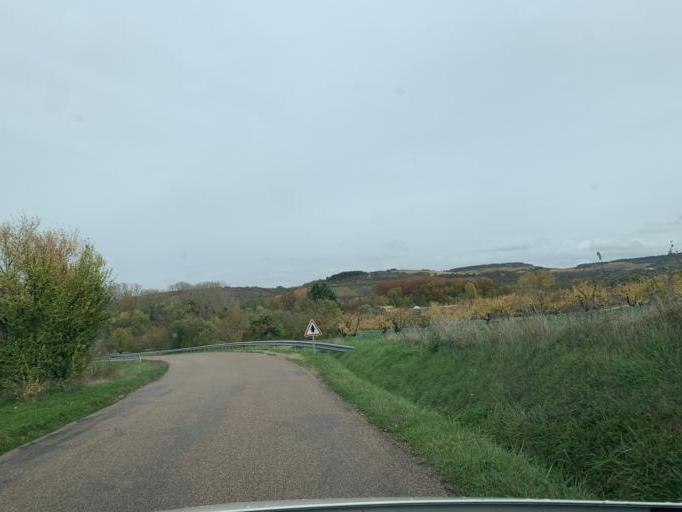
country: FR
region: Bourgogne
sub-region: Departement de l'Yonne
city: Champs-sur-Yonne
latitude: 47.7246
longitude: 3.5978
